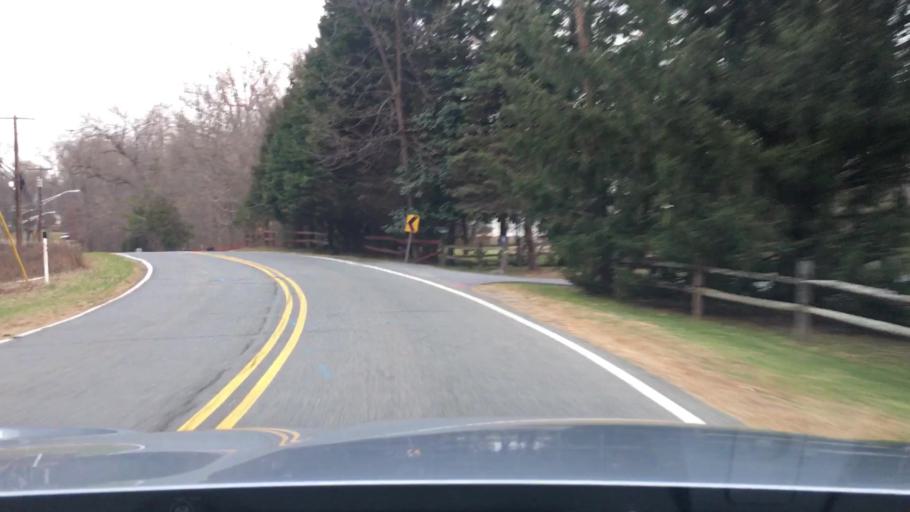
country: US
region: Maryland
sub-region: Prince George's County
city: Glenn Dale
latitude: 38.9942
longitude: -76.7746
